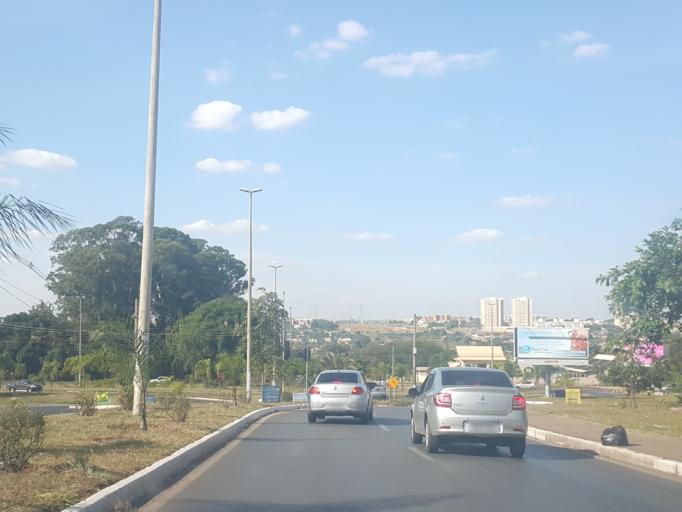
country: BR
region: Federal District
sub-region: Brasilia
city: Brasilia
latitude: -15.8349
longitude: -48.0067
